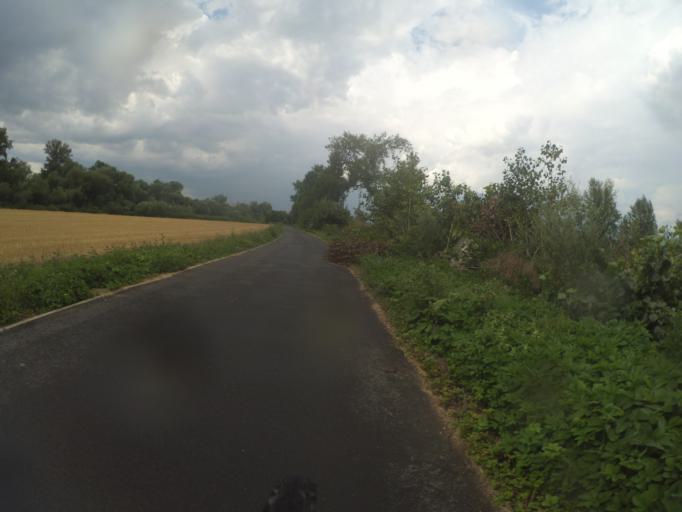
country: CZ
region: Central Bohemia
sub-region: Okres Melnik
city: Melnik
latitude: 50.3639
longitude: 14.4554
